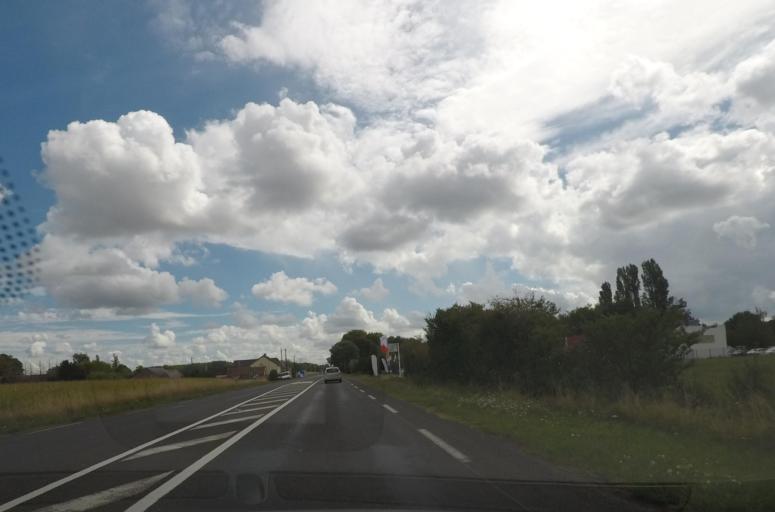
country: FR
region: Pays de la Loire
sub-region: Departement de la Sarthe
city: Bazouges-sur-le-Loir
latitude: 47.6907
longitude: -0.1556
